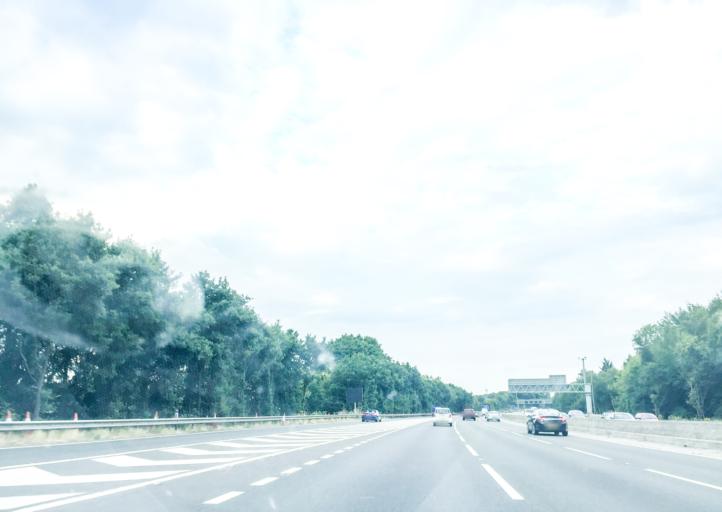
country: GB
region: England
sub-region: Surrey
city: Bagshot
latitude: 51.3588
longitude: -0.6730
